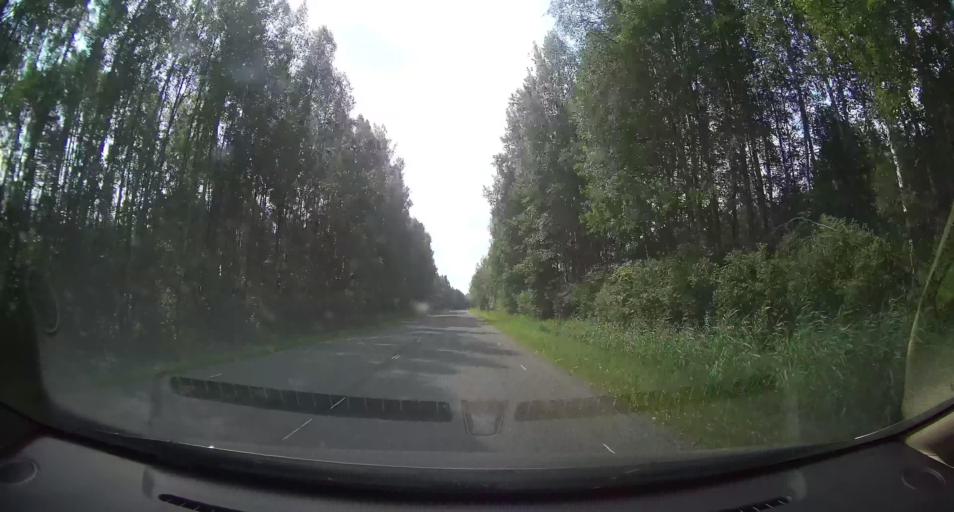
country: EE
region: Paernumaa
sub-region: Audru vald
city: Audru
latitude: 58.5117
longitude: 24.3611
